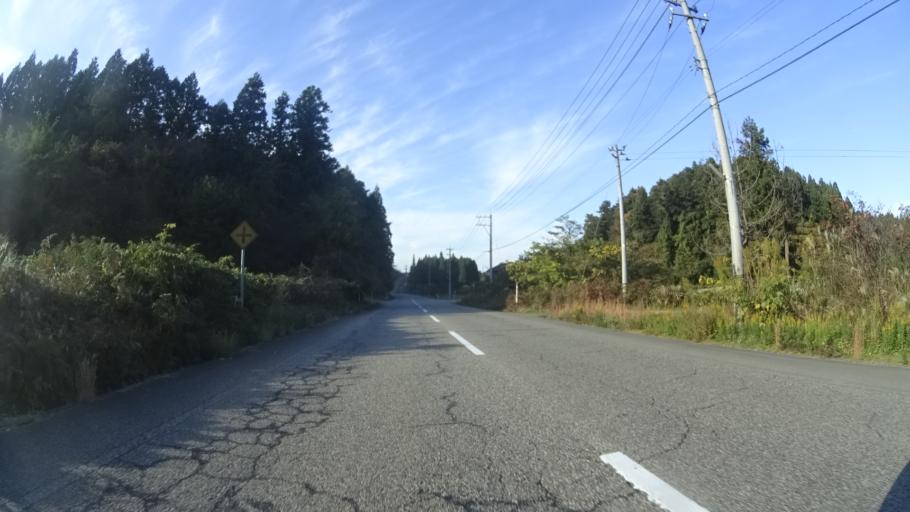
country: JP
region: Ishikawa
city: Hakui
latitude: 37.0146
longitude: 136.7962
